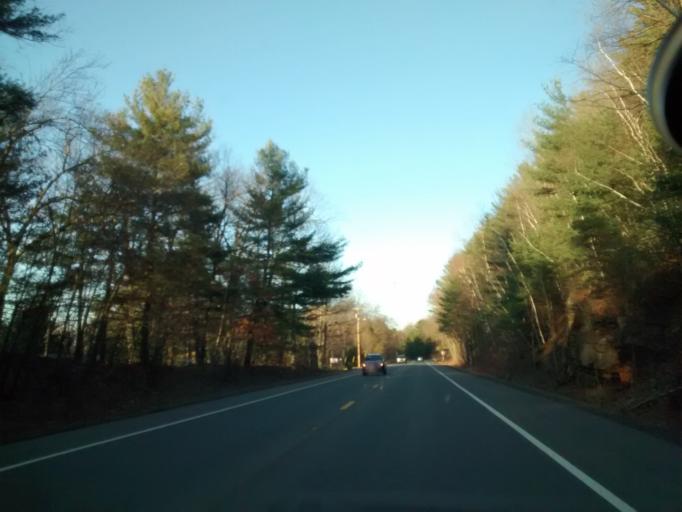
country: US
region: Massachusetts
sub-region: Worcester County
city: Warren
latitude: 42.2202
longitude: -72.1761
